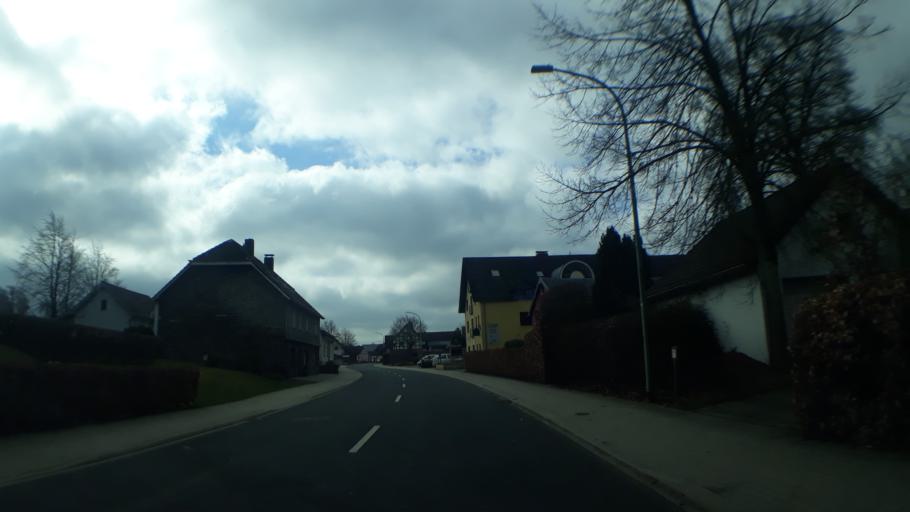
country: DE
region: North Rhine-Westphalia
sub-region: Regierungsbezirk Koln
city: Monschau
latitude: 50.5186
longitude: 6.2184
